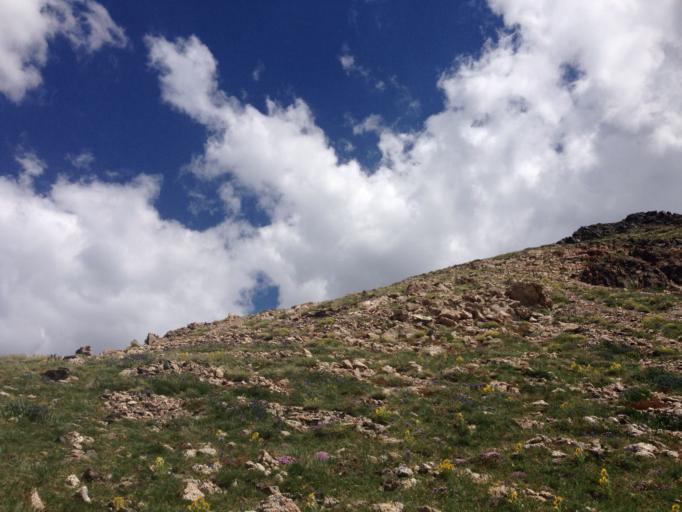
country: US
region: Colorado
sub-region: Larimer County
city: Estes Park
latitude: 40.4937
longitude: -105.8907
